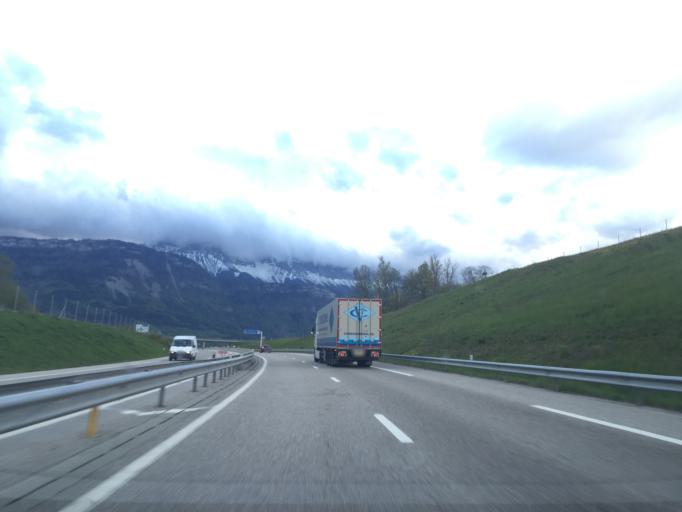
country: FR
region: Rhone-Alpes
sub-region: Departement de l'Isere
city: La Motte-Saint-Martin
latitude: 44.9580
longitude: 5.6543
